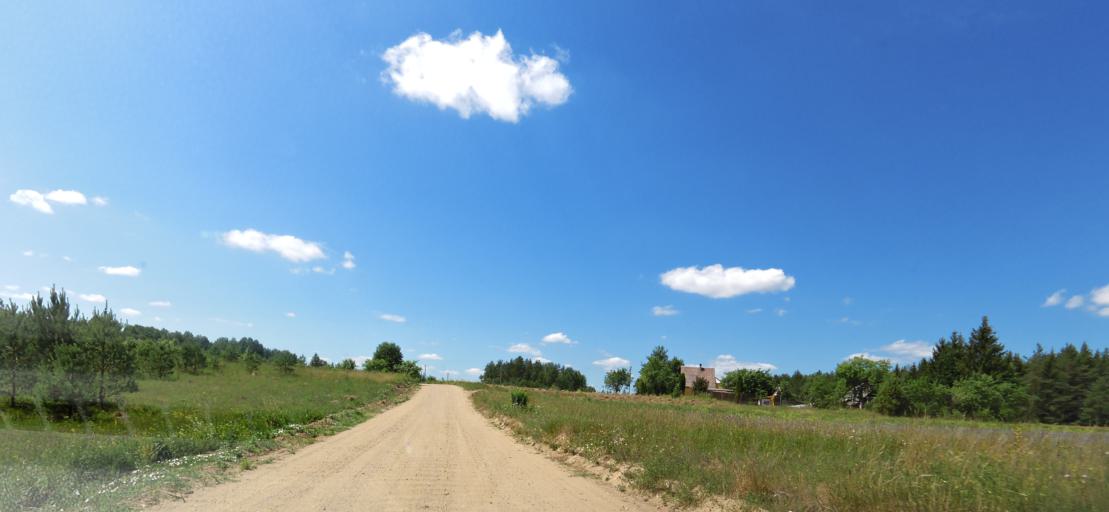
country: LT
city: Nemencine
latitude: 54.8718
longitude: 25.5612
